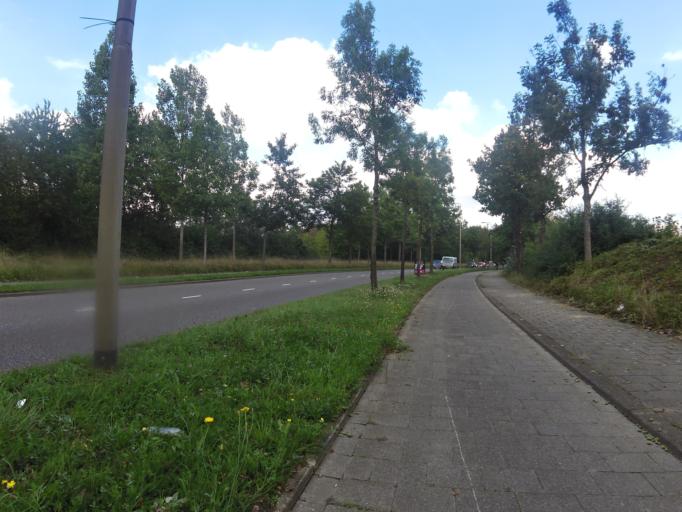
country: NL
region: Limburg
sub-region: Gemeente Heerlen
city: Nieuw-Lotbroek
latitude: 50.9119
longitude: 5.9456
